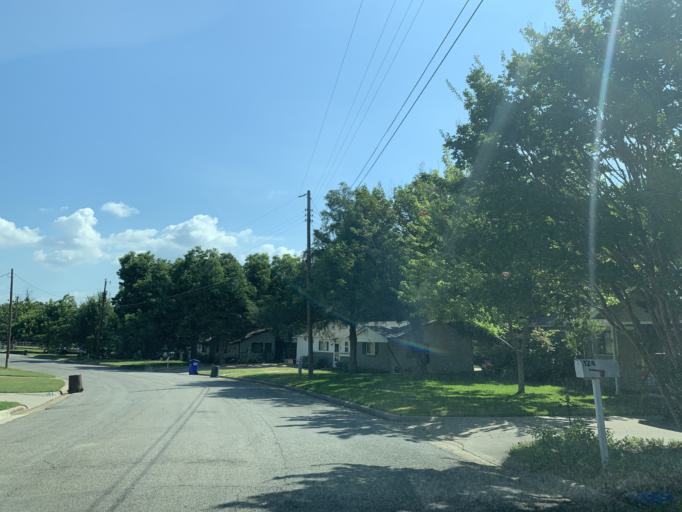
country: US
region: Texas
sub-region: Tarrant County
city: Azle
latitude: 32.8706
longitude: -97.5232
